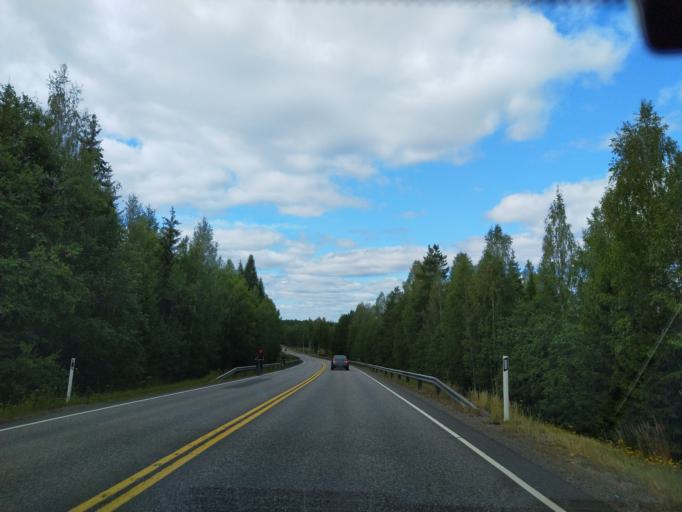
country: FI
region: Haeme
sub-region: Riihimaeki
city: Loppi
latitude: 60.7470
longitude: 24.3406
